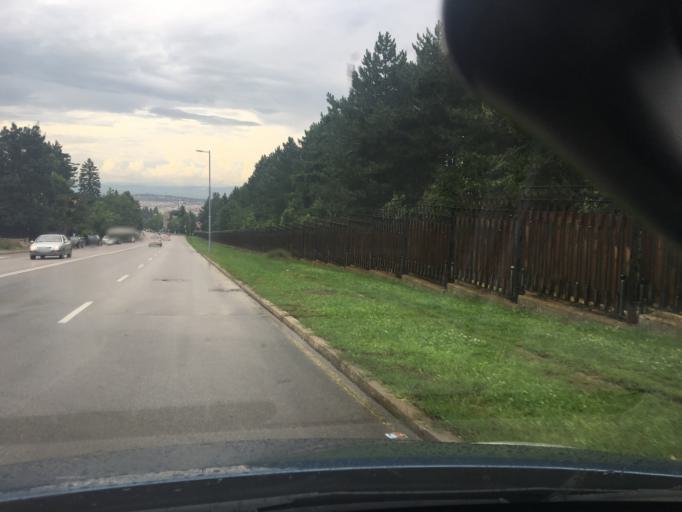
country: BG
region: Sofia-Capital
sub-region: Stolichna Obshtina
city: Sofia
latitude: 42.6522
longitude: 23.2662
